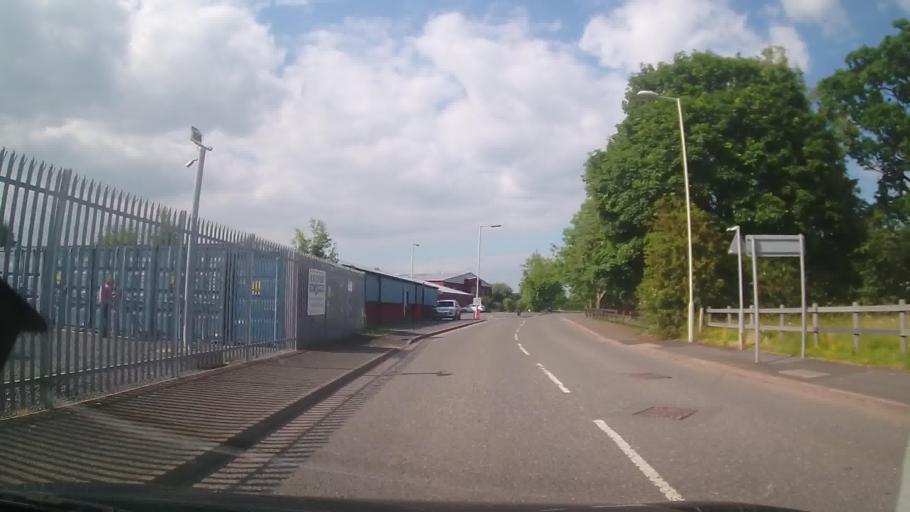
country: GB
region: England
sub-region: Shropshire
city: Craven Arms
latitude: 52.4461
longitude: -2.8421
